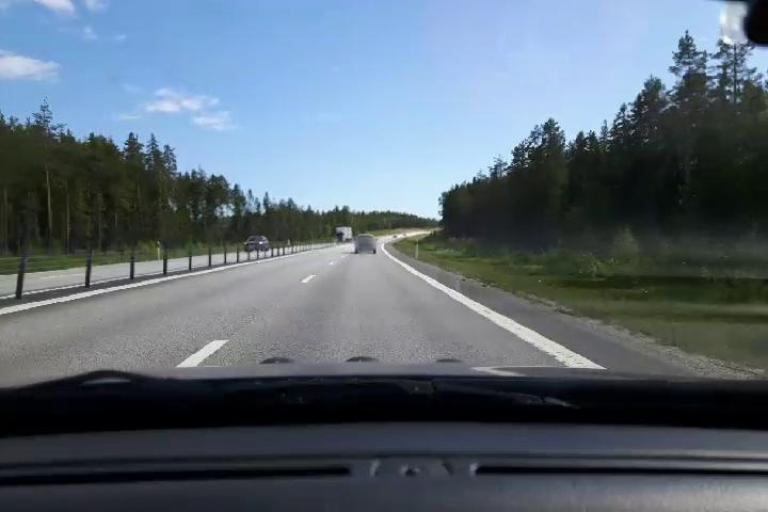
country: SE
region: Gaevleborg
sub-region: Hudiksvalls Kommun
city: Hudiksvall
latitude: 61.7004
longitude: 17.0550
